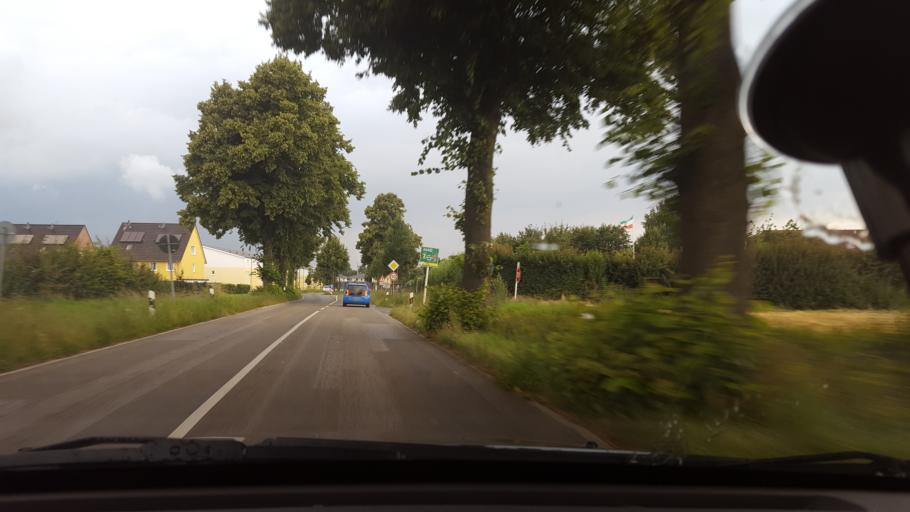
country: DE
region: North Rhine-Westphalia
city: Herten
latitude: 51.6531
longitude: 7.1489
